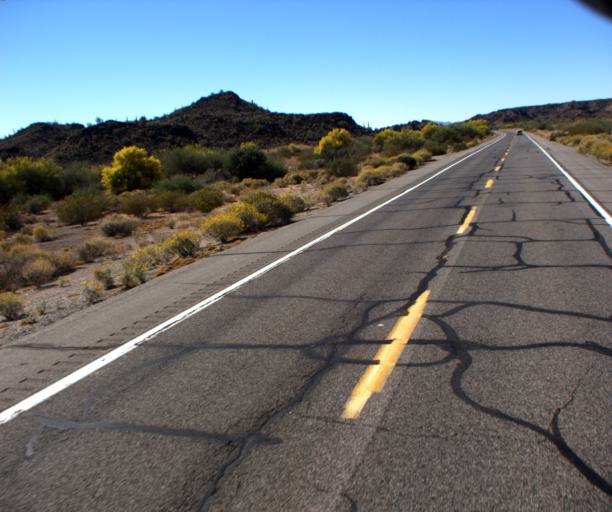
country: US
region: Arizona
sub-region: Pima County
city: Ajo
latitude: 32.5628
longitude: -112.8776
